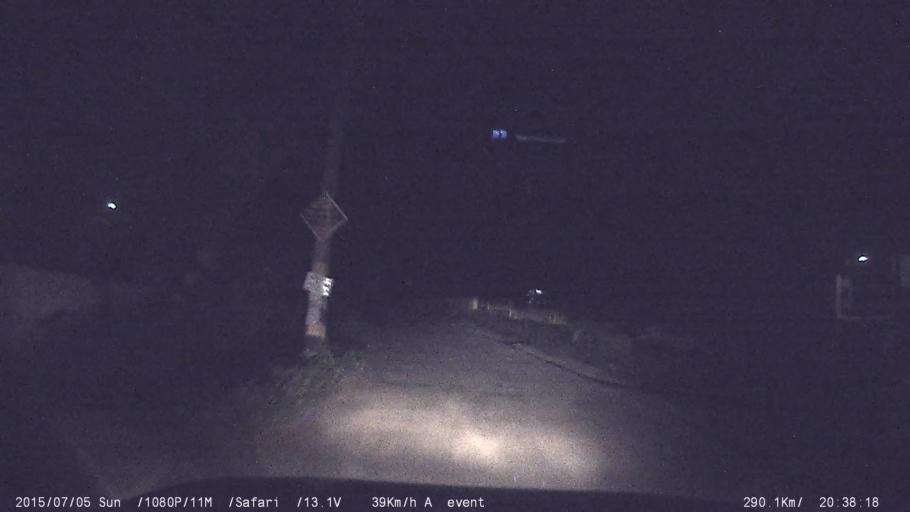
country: IN
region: Kerala
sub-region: Palakkad district
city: Mannarakkat
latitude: 10.9852
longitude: 76.4956
